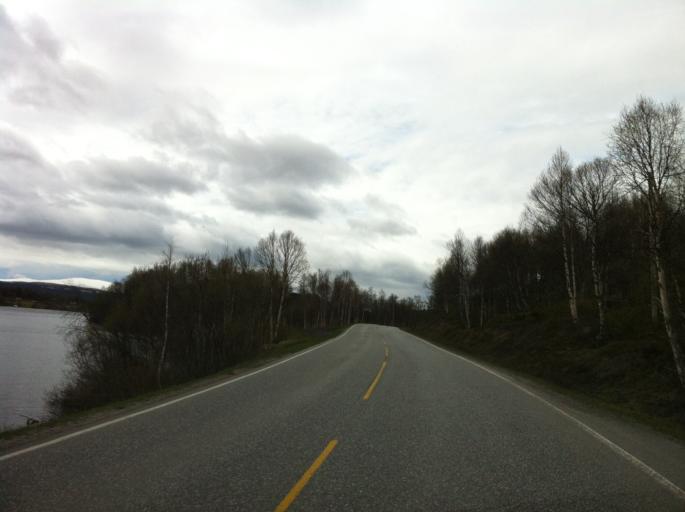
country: NO
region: Sor-Trondelag
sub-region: Roros
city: Roros
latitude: 62.5919
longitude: 11.4112
